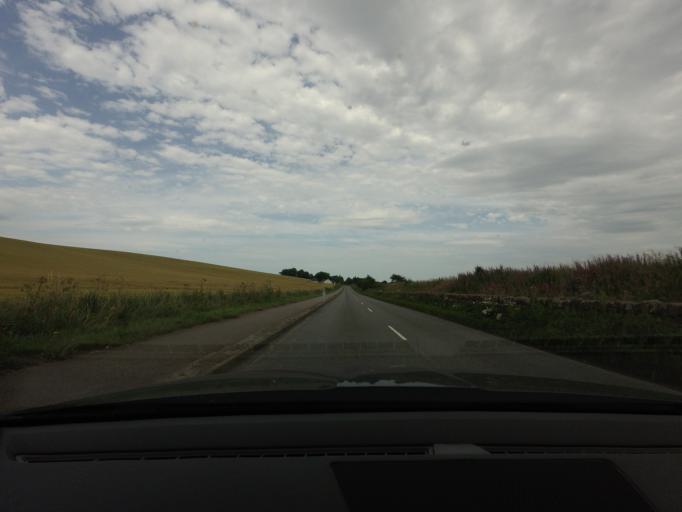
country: GB
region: Scotland
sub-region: Highland
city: Alness
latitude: 57.6869
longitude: -4.2835
